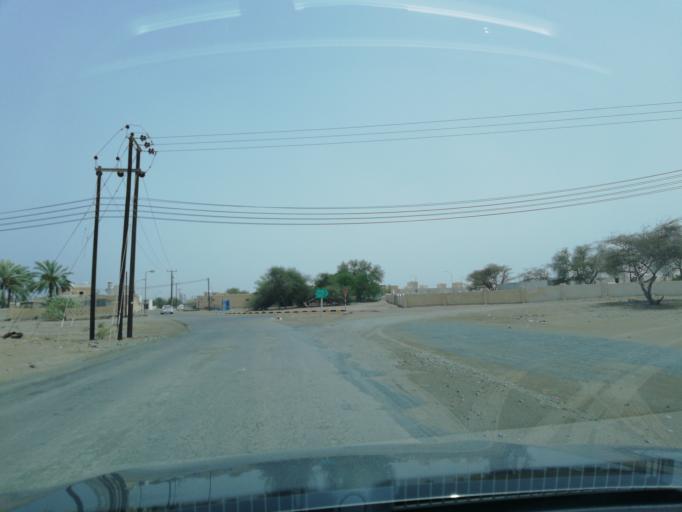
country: OM
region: Al Batinah
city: Al Liwa'
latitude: 24.6179
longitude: 56.5343
